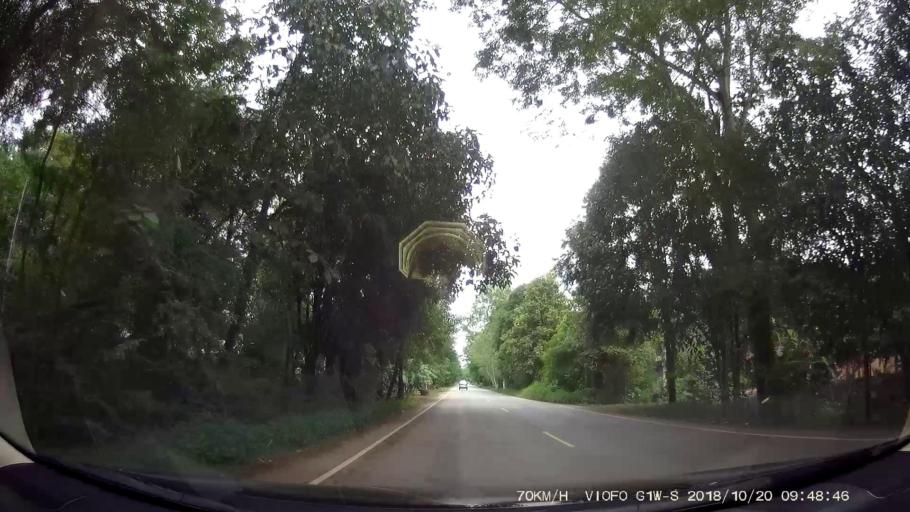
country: TH
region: Chaiyaphum
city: Khon San
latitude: 16.5139
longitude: 101.9095
